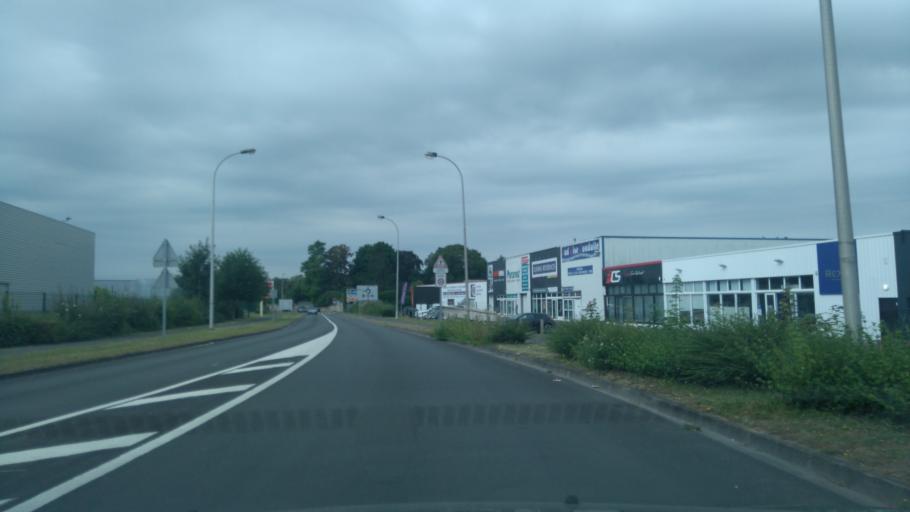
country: FR
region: Picardie
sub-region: Departement de l'Oise
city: Saint-Maximin
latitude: 49.2383
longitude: 2.4633
